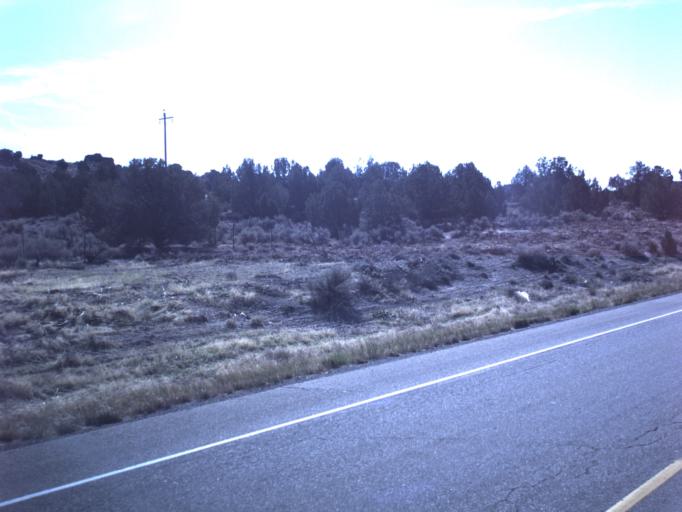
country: US
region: Utah
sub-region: Sanpete County
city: Gunnison
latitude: 39.3689
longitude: -111.9293
